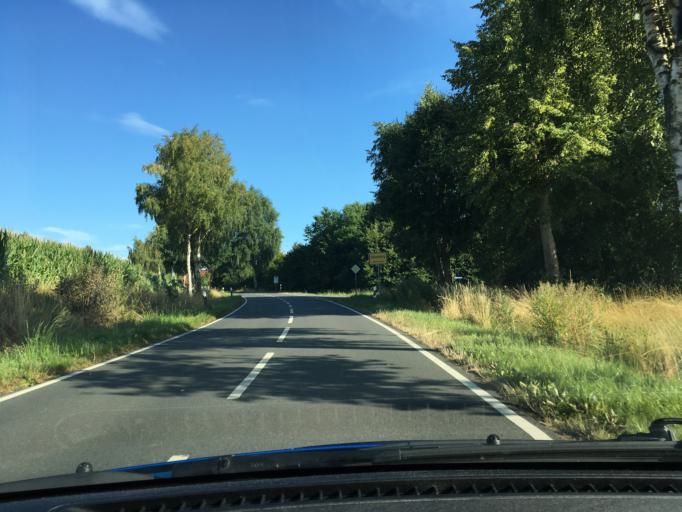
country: DE
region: Lower Saxony
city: Dahlenburg
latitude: 53.1927
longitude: 10.7208
